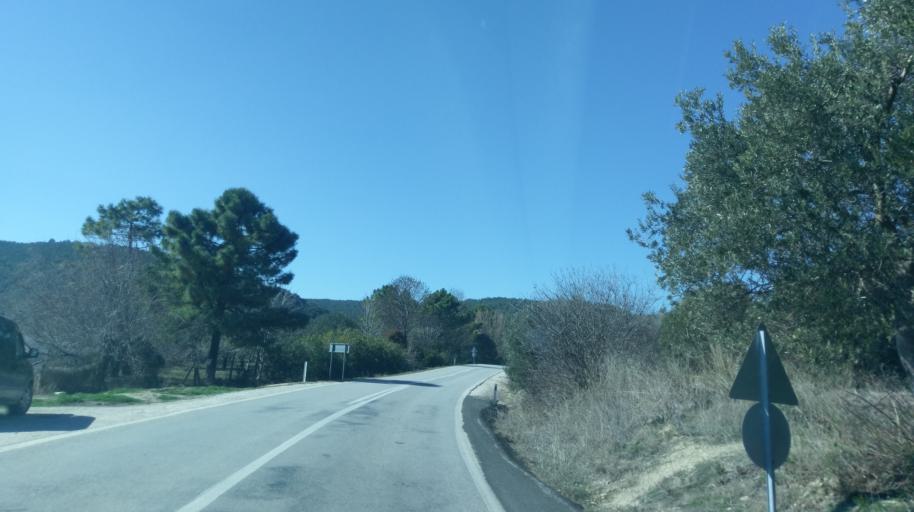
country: TR
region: Canakkale
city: Eceabat
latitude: 40.1031
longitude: 26.3194
